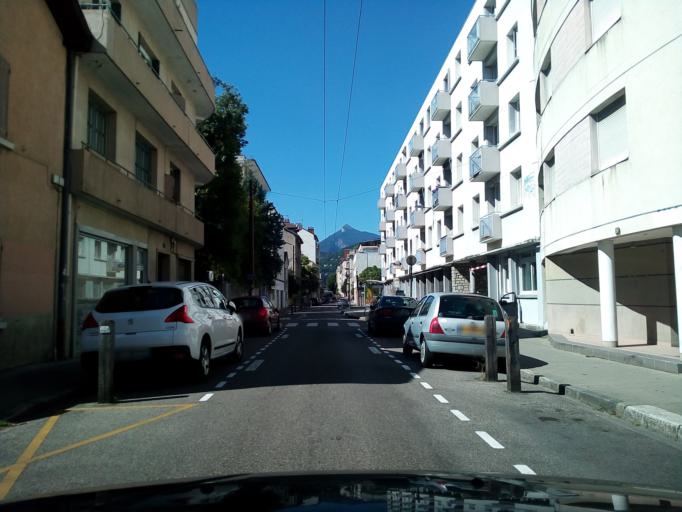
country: FR
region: Rhone-Alpes
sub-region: Departement de l'Isere
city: Grenoble
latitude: 45.1835
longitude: 5.7117
